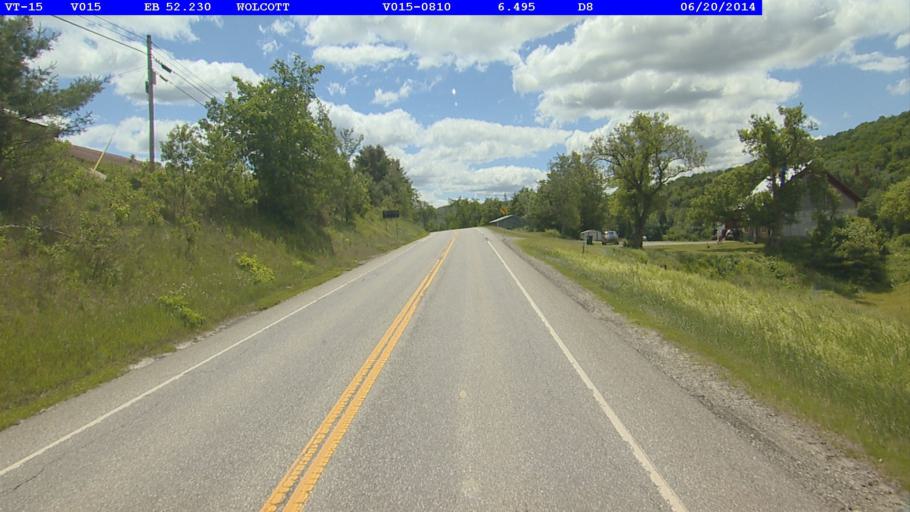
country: US
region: Vermont
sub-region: Caledonia County
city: Hardwick
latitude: 44.5312
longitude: -72.4250
